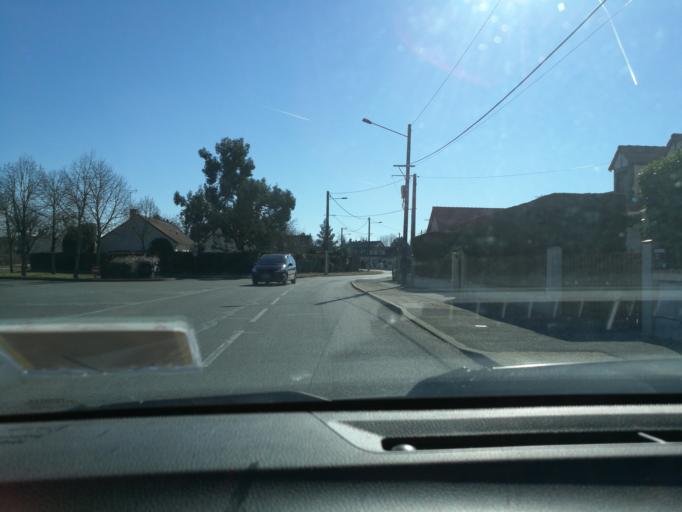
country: FR
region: Centre
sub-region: Departement du Loiret
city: Saint-Jean-le-Blanc
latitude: 47.8797
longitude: 1.9191
